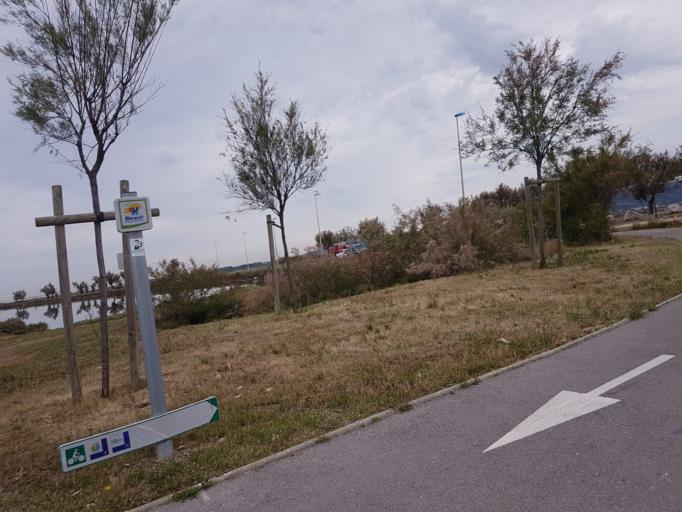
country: FR
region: Languedoc-Roussillon
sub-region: Departement de l'Herault
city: Frontignan
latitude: 43.4410
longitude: 3.7917
